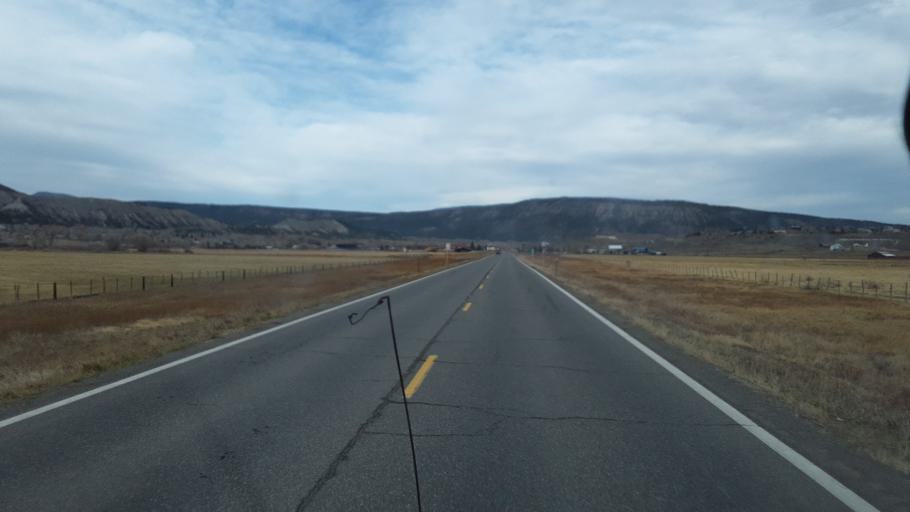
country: US
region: Colorado
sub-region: Ouray County
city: Ouray
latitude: 38.1430
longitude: -107.7396
